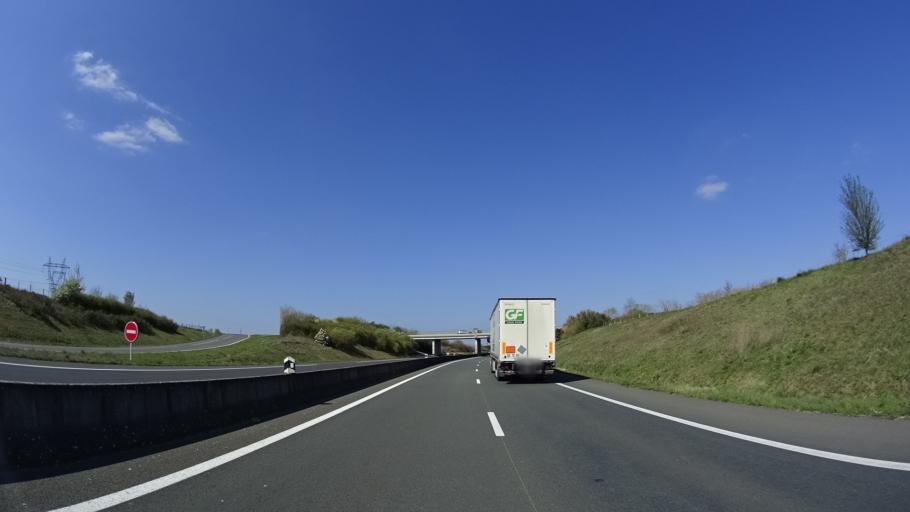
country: FR
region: Pays de la Loire
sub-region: Departement de Maine-et-Loire
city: Doue-la-Fontaine
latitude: 47.2345
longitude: -0.3169
